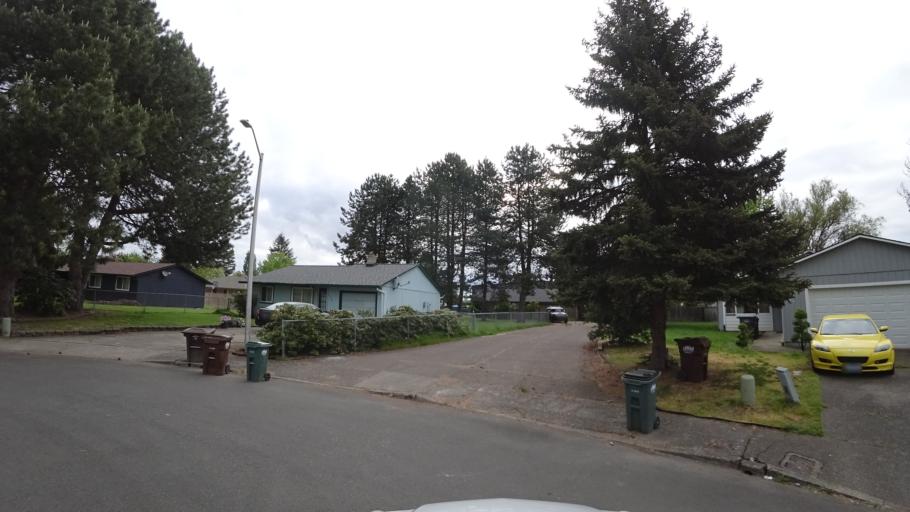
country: US
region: Oregon
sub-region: Washington County
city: Hillsboro
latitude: 45.5358
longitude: -122.9598
